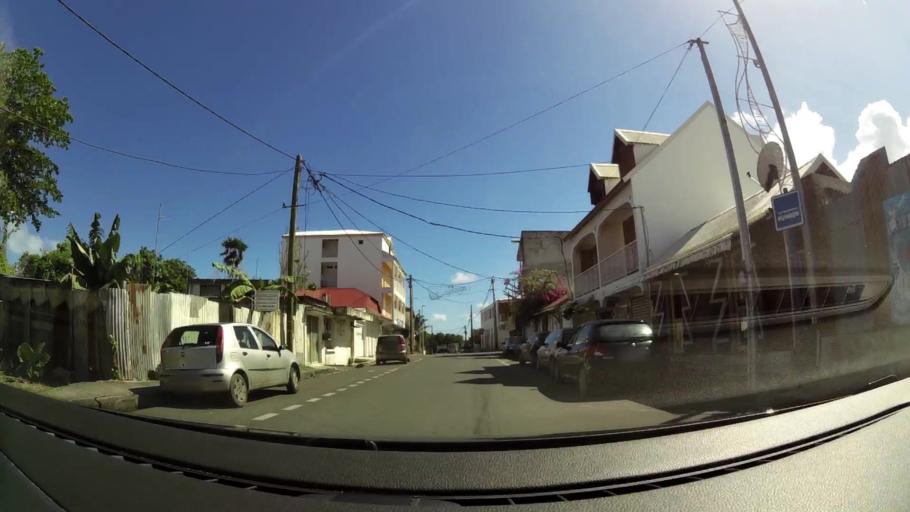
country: GP
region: Guadeloupe
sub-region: Guadeloupe
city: Le Moule
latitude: 16.3296
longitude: -61.3440
